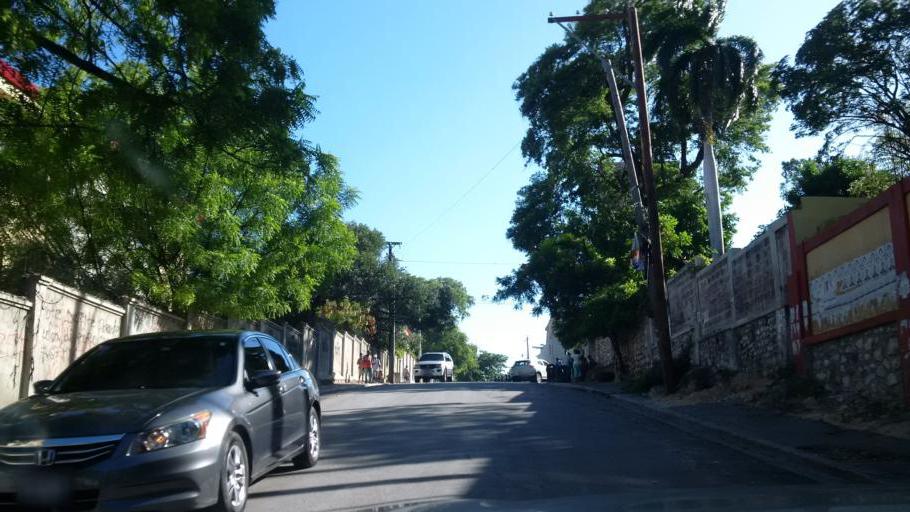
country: HT
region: Ouest
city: Port-au-Prince
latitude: 18.5391
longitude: -72.3188
